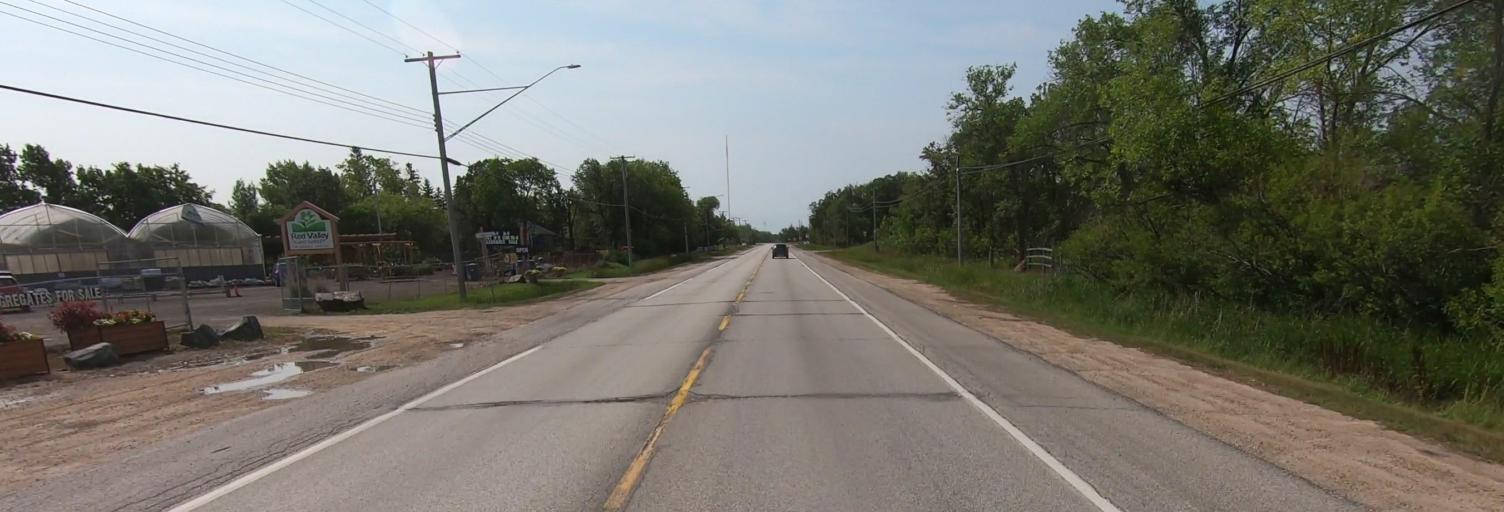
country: CA
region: Manitoba
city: Winnipeg
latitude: 49.7726
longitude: -97.1273
